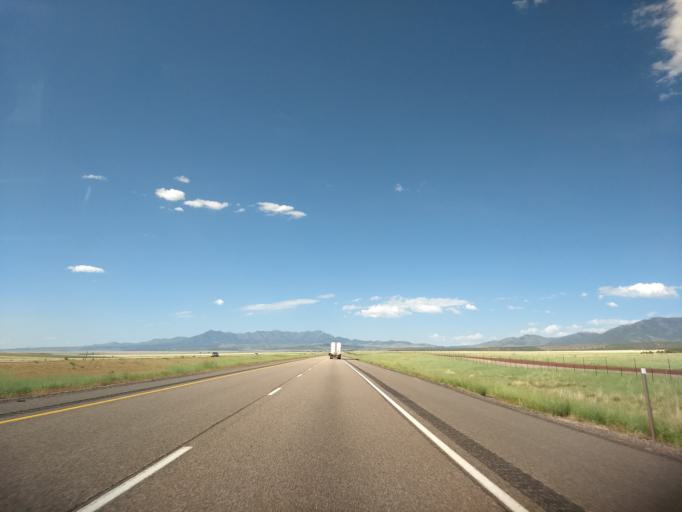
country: US
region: Utah
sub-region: Millard County
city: Fillmore
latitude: 39.0261
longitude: -112.3011
